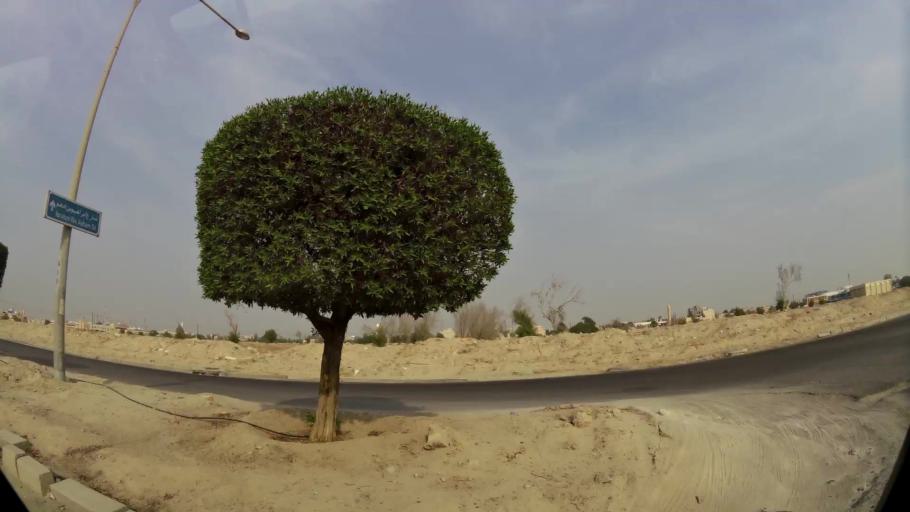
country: KW
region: Al Farwaniyah
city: Janub as Surrah
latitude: 29.2733
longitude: 47.9792
